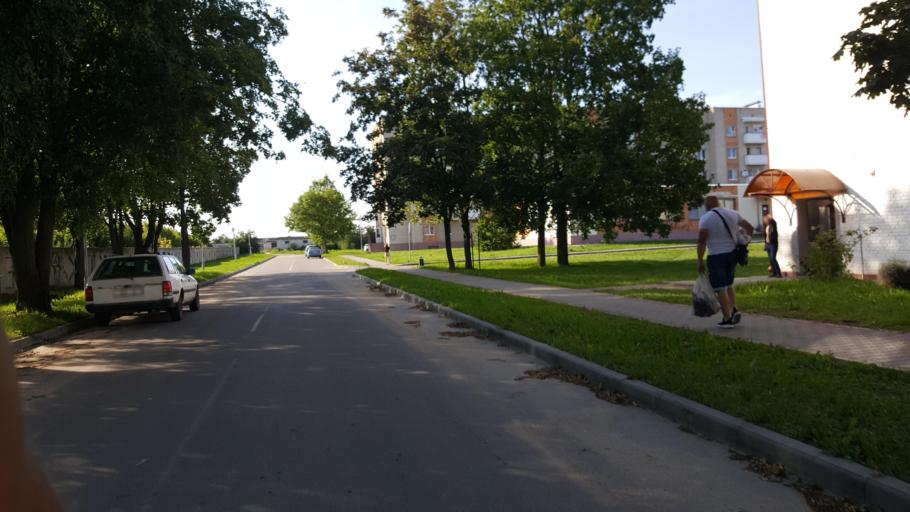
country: BY
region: Brest
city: Vysokaye
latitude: 52.3793
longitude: 23.3651
